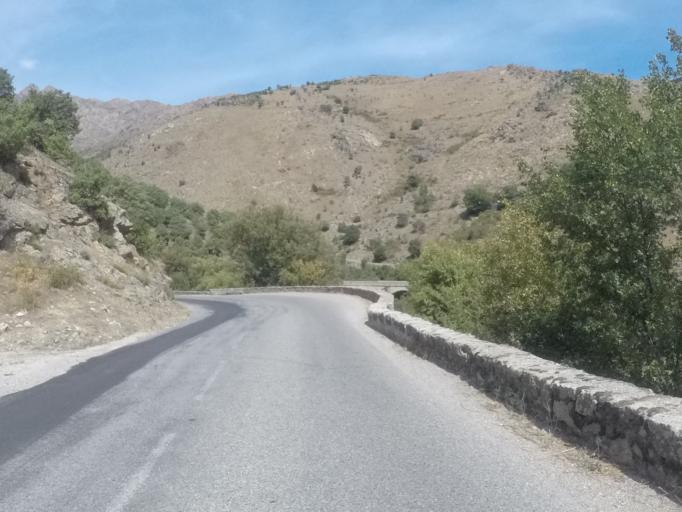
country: FR
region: Corsica
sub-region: Departement de la Haute-Corse
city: Corte
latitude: 42.3443
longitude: 9.0335
